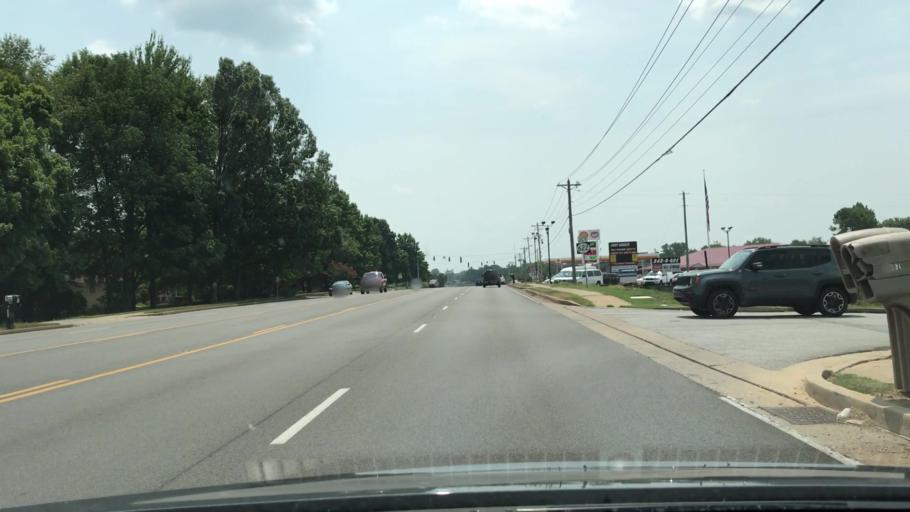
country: US
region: Kentucky
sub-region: Warren County
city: Plano
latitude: 36.9219
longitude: -86.4097
